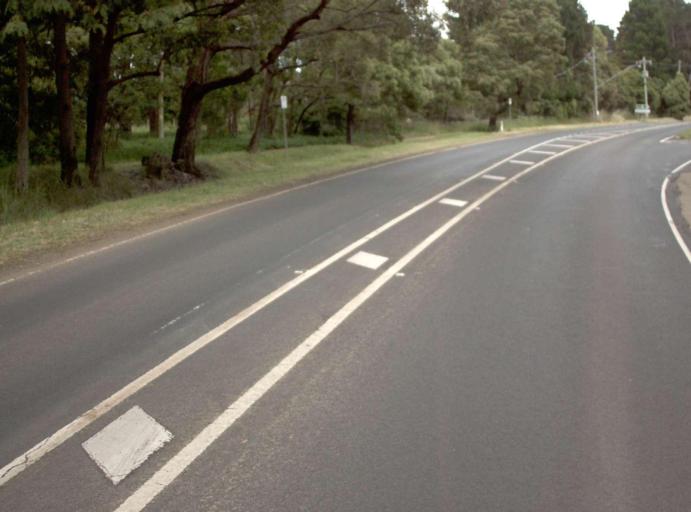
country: AU
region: Victoria
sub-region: Mornington Peninsula
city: Safety Beach
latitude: -38.3696
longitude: 145.0064
